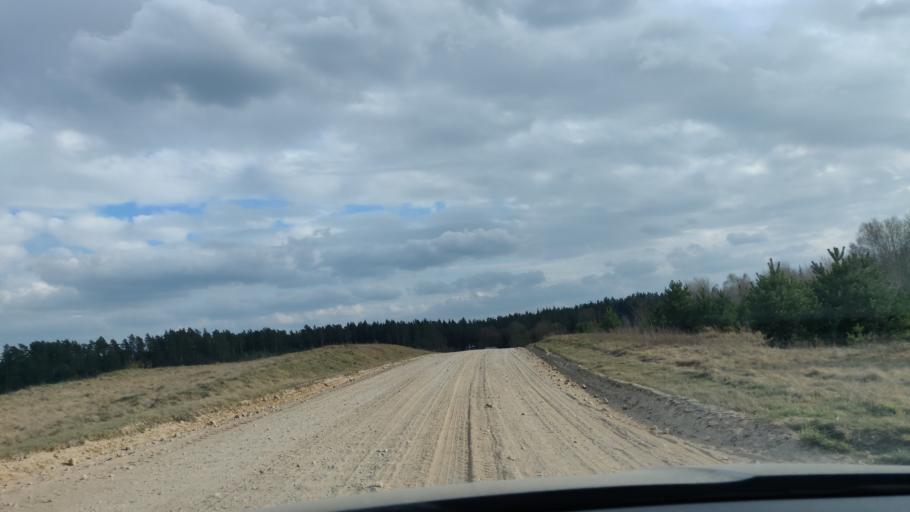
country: LT
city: Lentvaris
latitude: 54.6066
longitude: 25.0745
